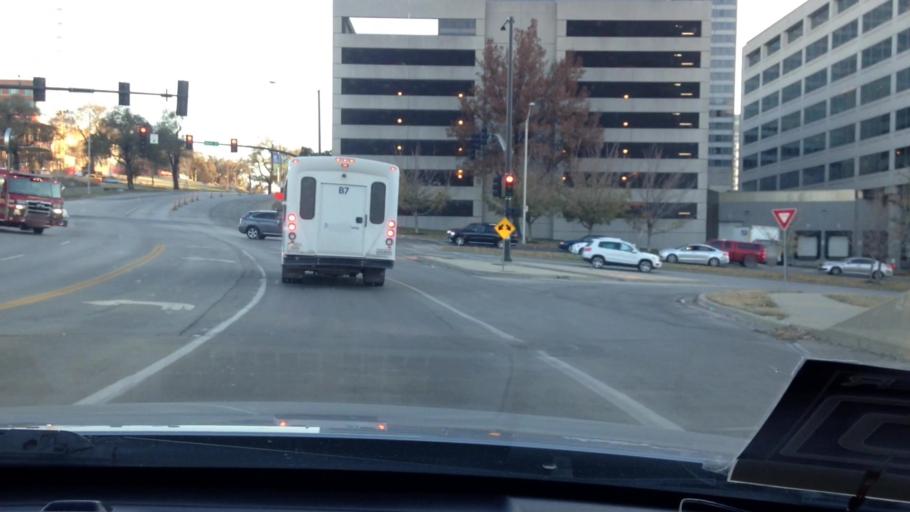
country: US
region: Missouri
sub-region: Jackson County
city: Kansas City
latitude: 39.0871
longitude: -94.5793
